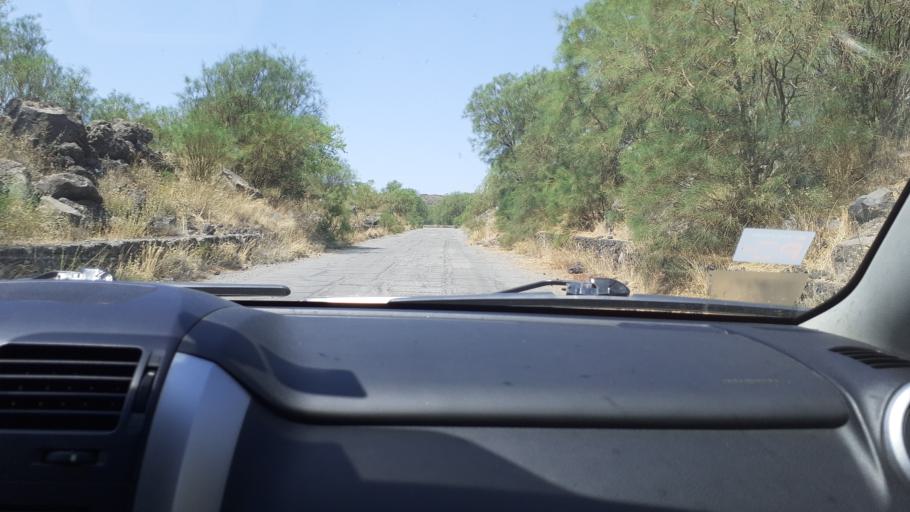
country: IT
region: Sicily
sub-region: Catania
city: Nicolosi
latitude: 37.6461
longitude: 15.0041
